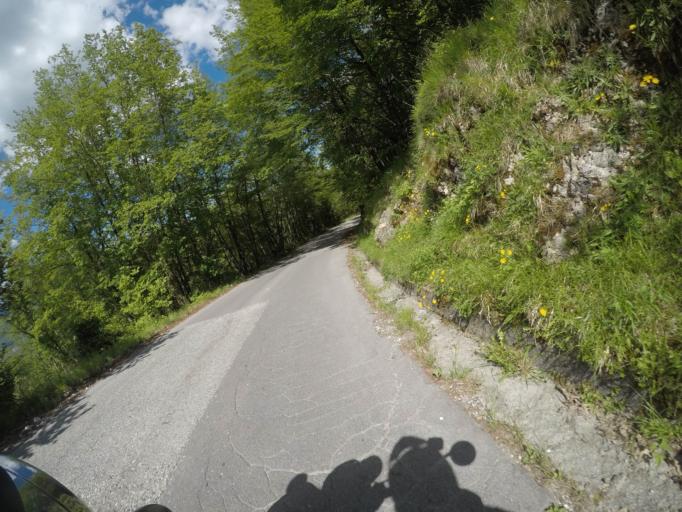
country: IT
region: Tuscany
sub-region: Provincia di Lucca
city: Minucciano
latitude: 44.1620
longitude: 10.2063
